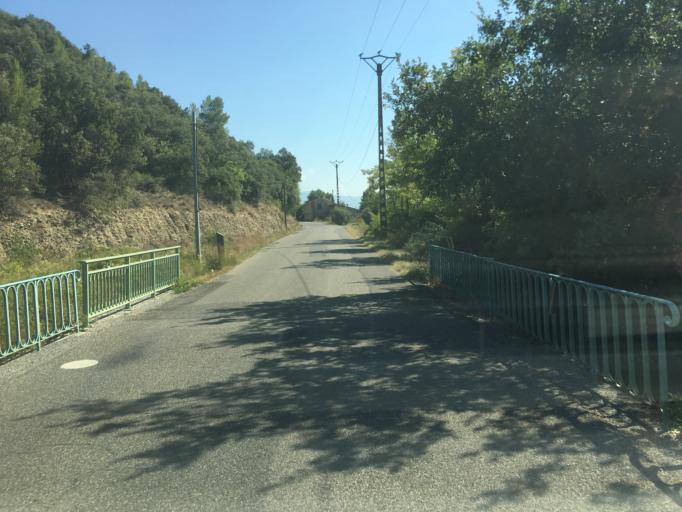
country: FR
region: Provence-Alpes-Cote d'Azur
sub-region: Departement des Alpes-de-Haute-Provence
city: Valensole
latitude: 43.8996
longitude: 6.0195
